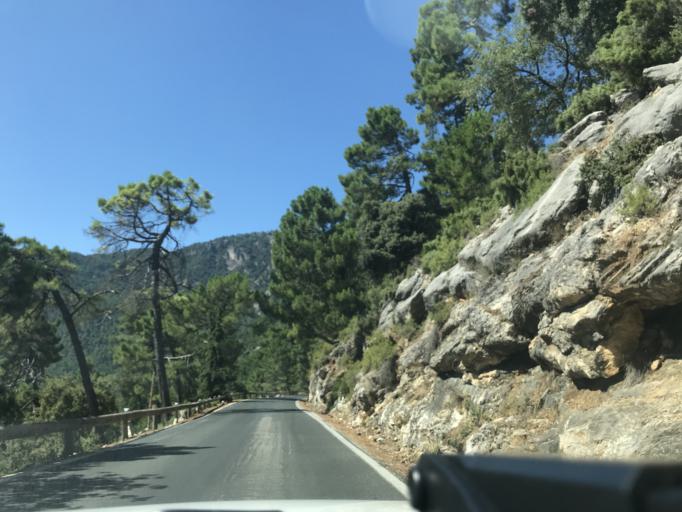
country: ES
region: Andalusia
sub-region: Provincia de Jaen
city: La Iruela
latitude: 37.9262
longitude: -2.9504
